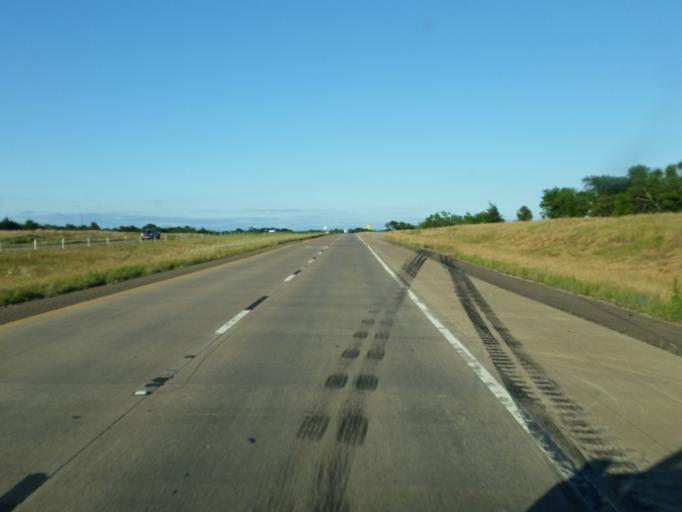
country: US
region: Texas
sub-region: Kaufman County
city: Talty
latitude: 32.6999
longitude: -96.3640
